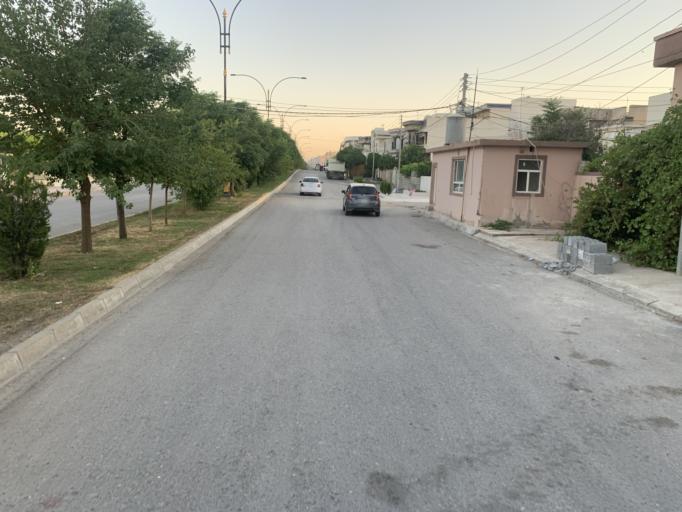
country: IQ
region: As Sulaymaniyah
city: Raniye
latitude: 36.2456
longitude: 44.8775
